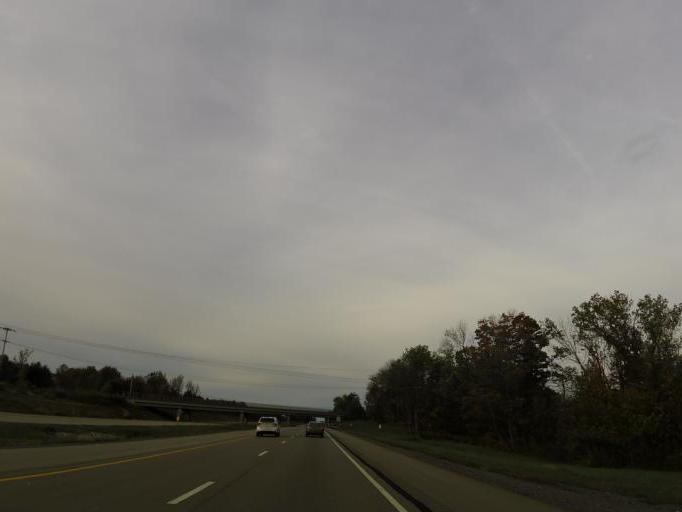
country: US
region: New York
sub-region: Erie County
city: Angola
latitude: 42.6302
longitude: -78.9965
